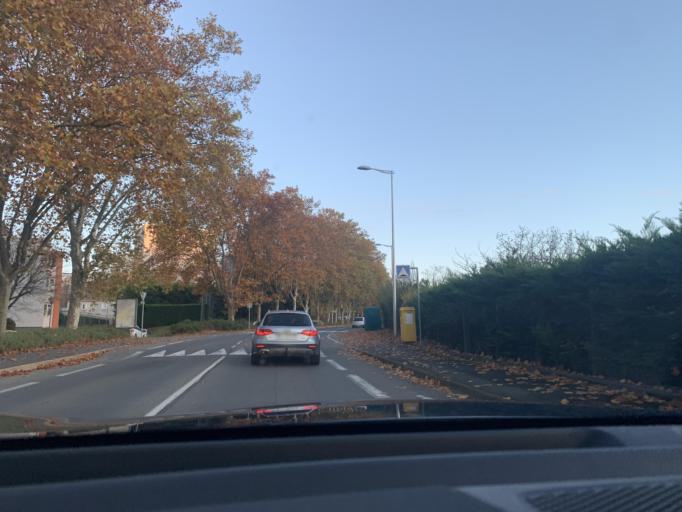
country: FR
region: Rhone-Alpes
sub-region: Departement du Rhone
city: Limas
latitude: 45.9812
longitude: 4.6962
